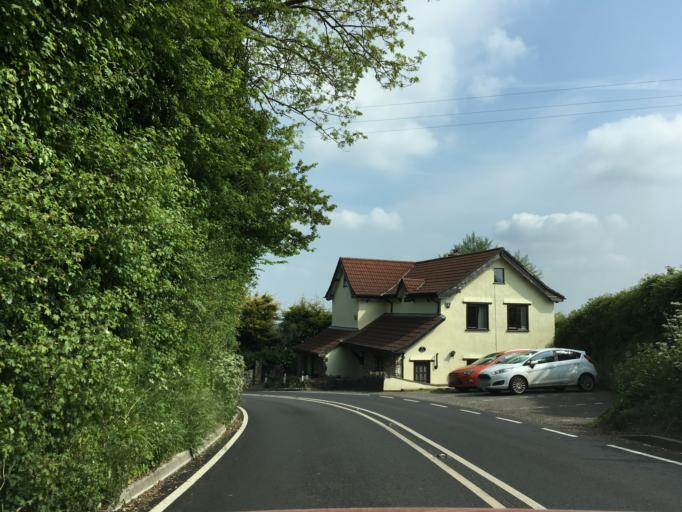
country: GB
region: England
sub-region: North Somerset
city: Dundry
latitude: 51.3999
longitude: -2.6247
